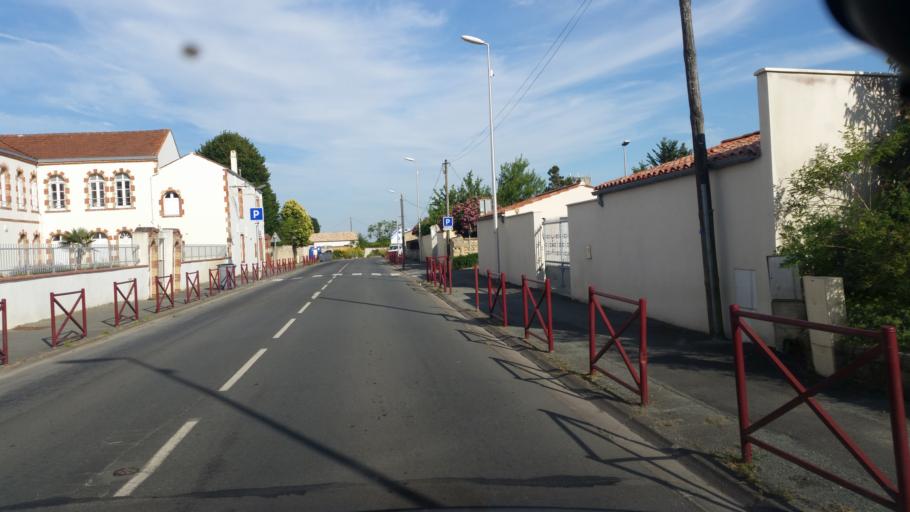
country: FR
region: Poitou-Charentes
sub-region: Departement de la Charente-Maritime
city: Marans
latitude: 46.3051
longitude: -0.9883
